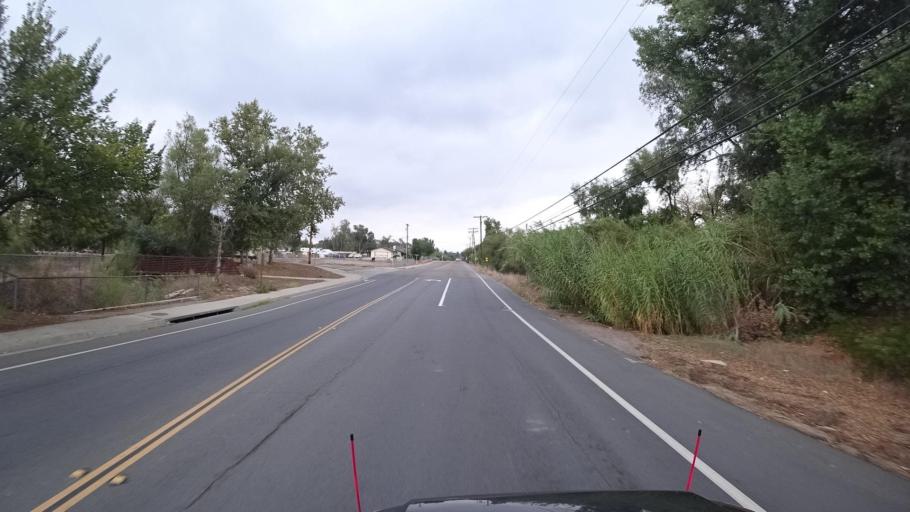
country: US
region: California
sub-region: San Diego County
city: Ramona
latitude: 33.0304
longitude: -116.8795
